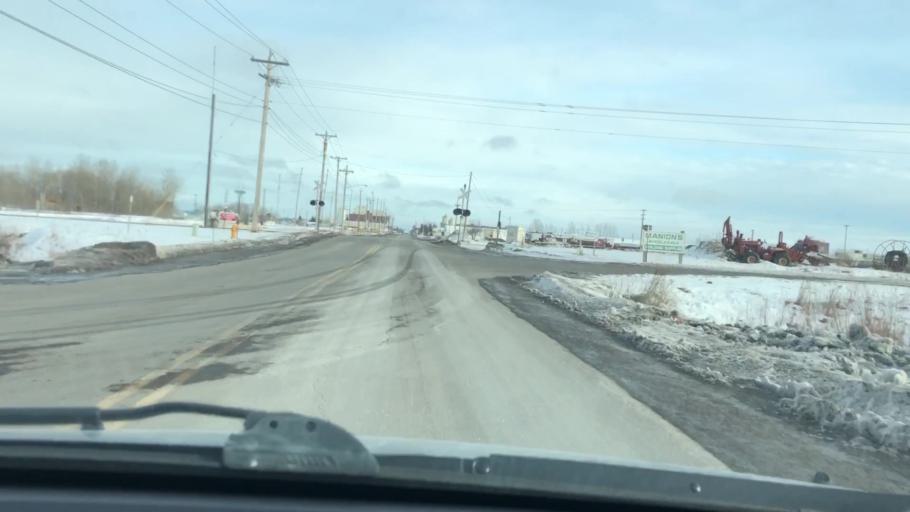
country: US
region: Wisconsin
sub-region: Douglas County
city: Superior
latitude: 46.7279
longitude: -92.1163
